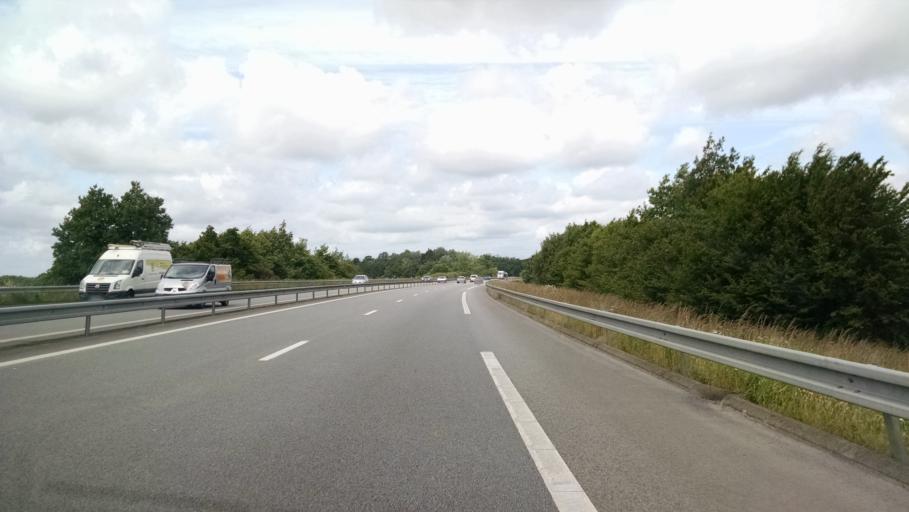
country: FR
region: Brittany
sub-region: Departement du Morbihan
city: Auray
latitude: 47.6618
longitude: -3.0085
